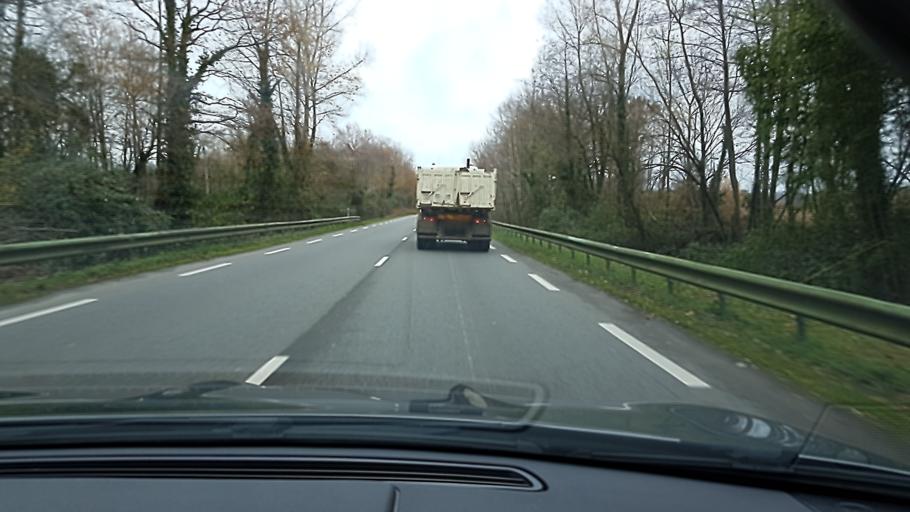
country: FR
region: Aquitaine
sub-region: Departement des Pyrenees-Atlantiques
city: Idron
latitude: 43.3101
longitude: -0.3057
